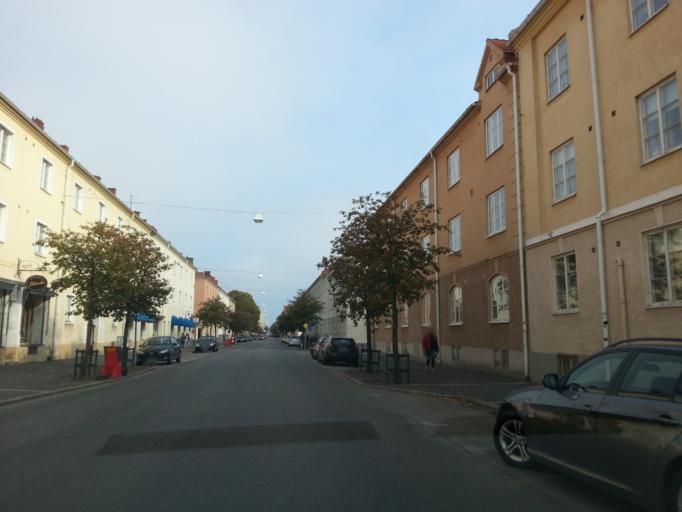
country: SE
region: Joenkoeping
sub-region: Jonkopings Kommun
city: Jonkoping
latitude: 57.7735
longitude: 14.1528
